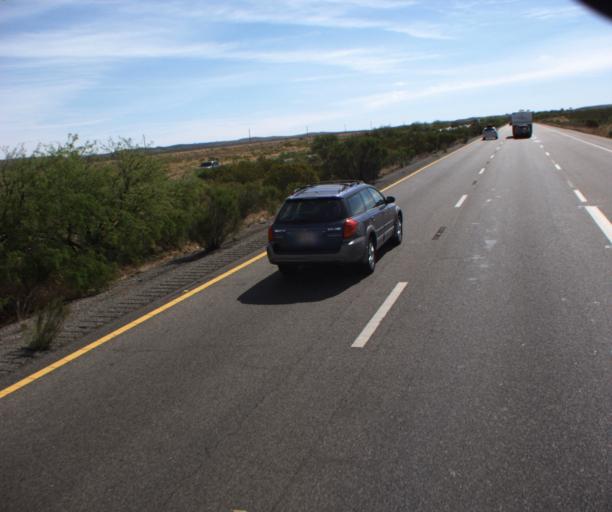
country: US
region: Arizona
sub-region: Cochise County
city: Mescal
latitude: 31.9806
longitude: -110.5300
